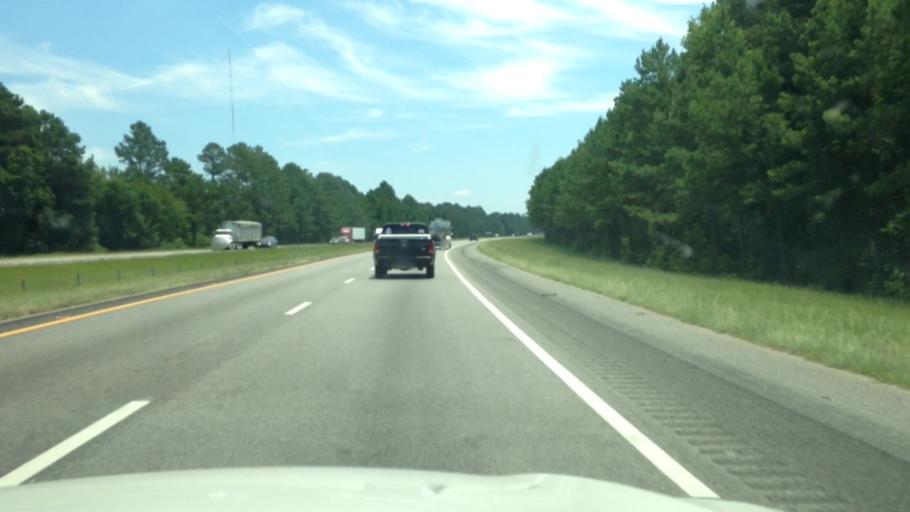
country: US
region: South Carolina
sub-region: Darlington County
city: Darlington
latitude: 34.2040
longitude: -79.8724
